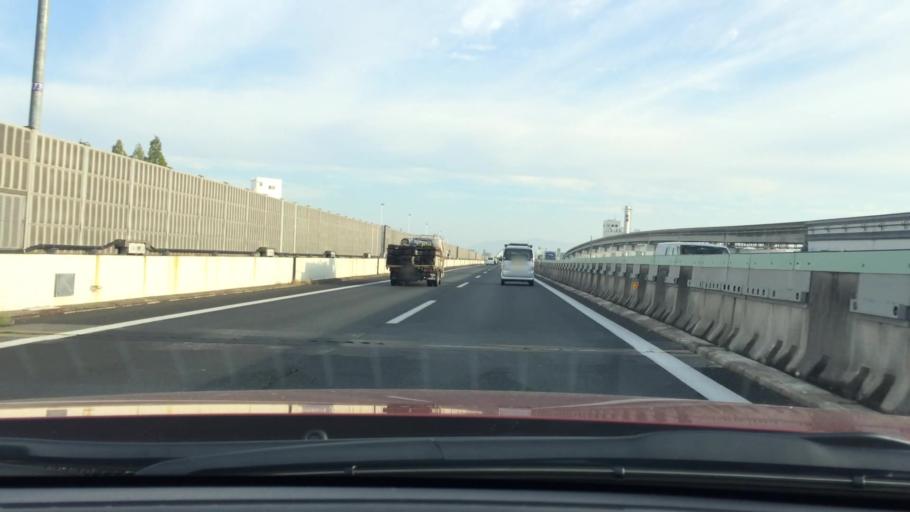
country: JP
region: Osaka
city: Ibaraki
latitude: 34.7866
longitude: 135.5632
